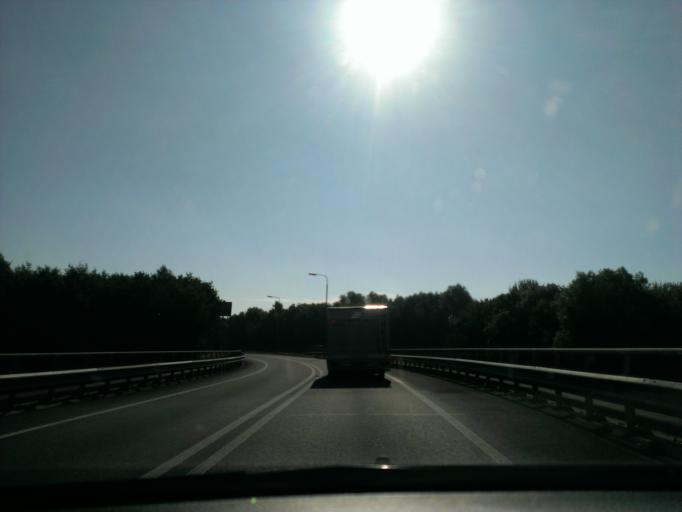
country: NL
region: Drenthe
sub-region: Gemeente Coevorden
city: Coevorden
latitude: 52.6768
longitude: 6.7292
